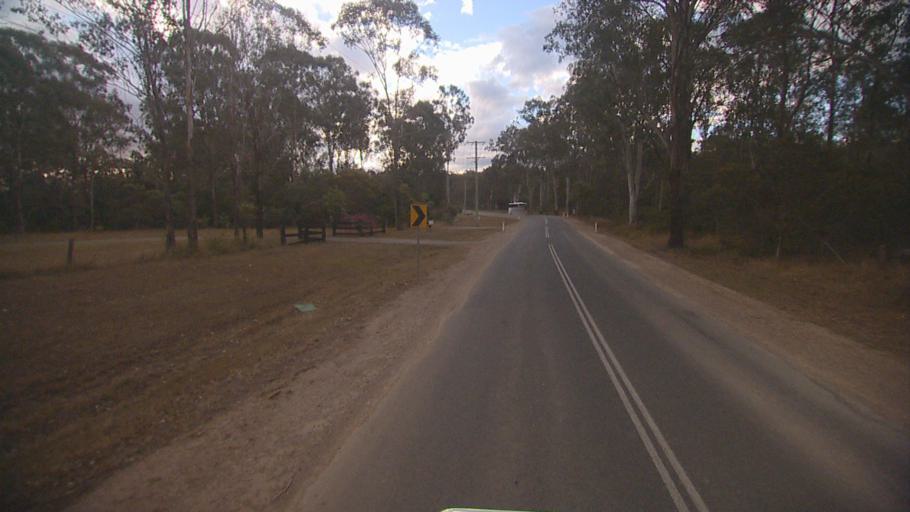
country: AU
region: Queensland
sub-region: Logan
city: Cedar Vale
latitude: -27.8483
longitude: 153.0508
